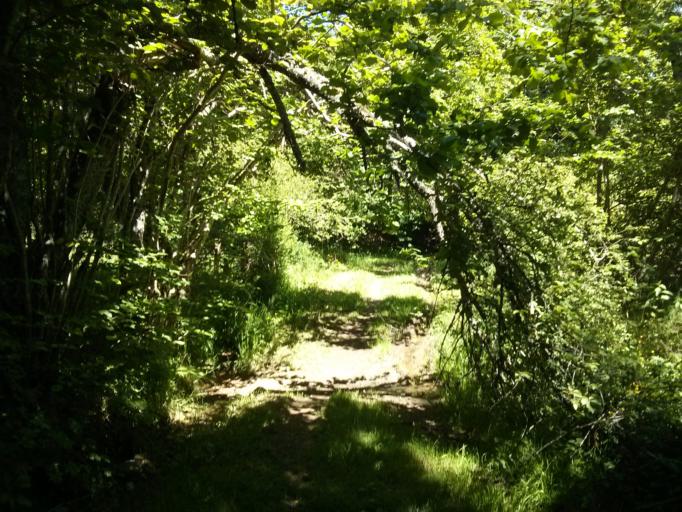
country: FR
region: Auvergne
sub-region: Departement du Puy-de-Dome
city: Mont-Dore
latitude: 45.5907
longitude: 2.8043
